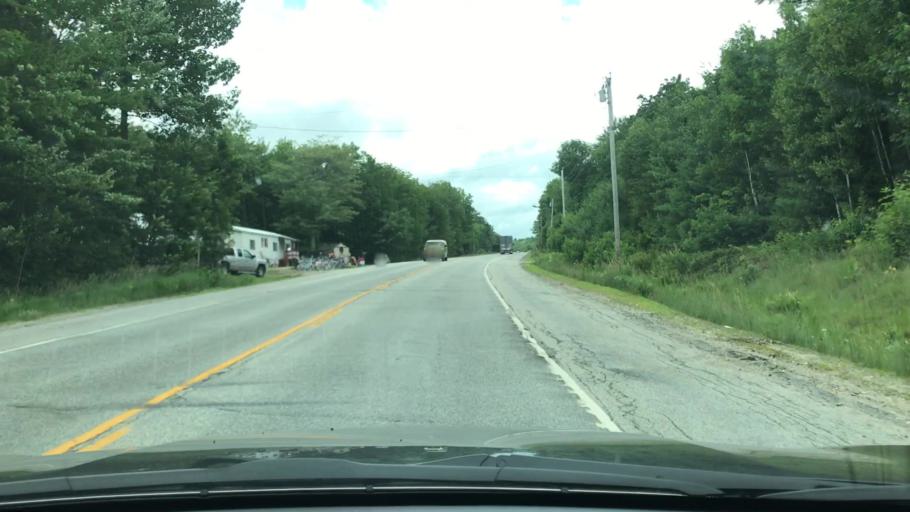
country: US
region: Maine
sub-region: Oxford County
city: West Paris
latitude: 44.3620
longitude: -70.5842
